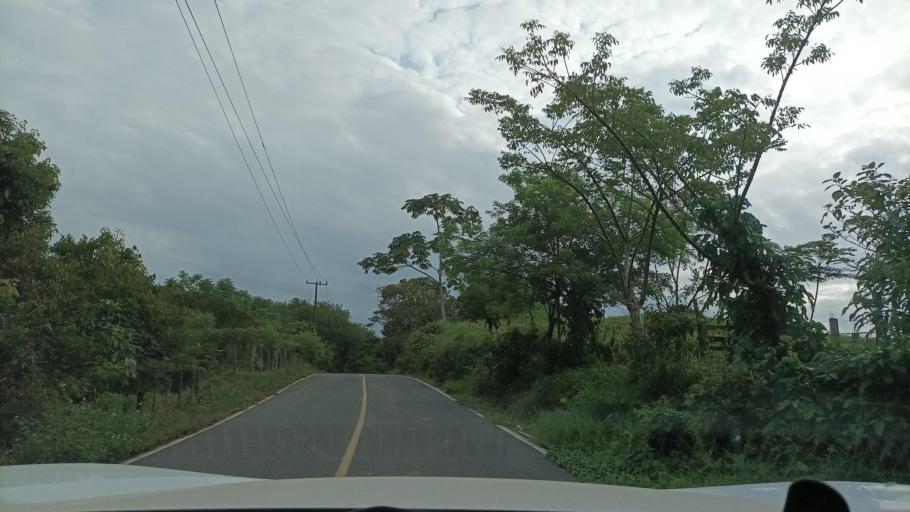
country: MX
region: Veracruz
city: Hidalgotitlan
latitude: 17.6900
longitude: -94.4582
